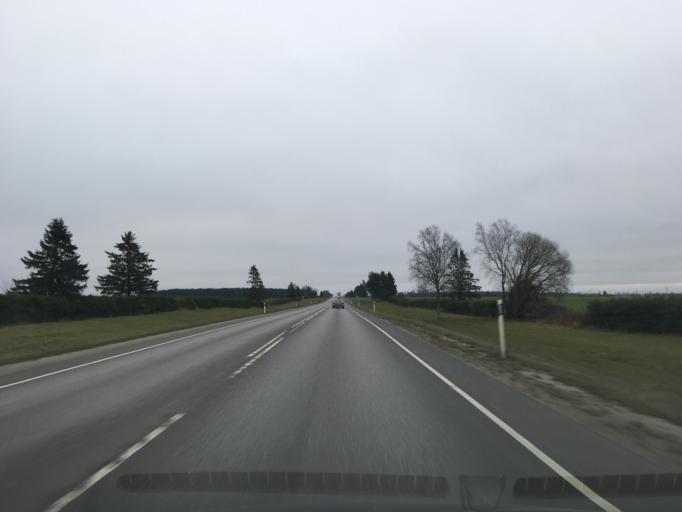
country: EE
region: Laeaene-Virumaa
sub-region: Haljala vald
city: Haljala
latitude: 59.4200
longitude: 26.3052
